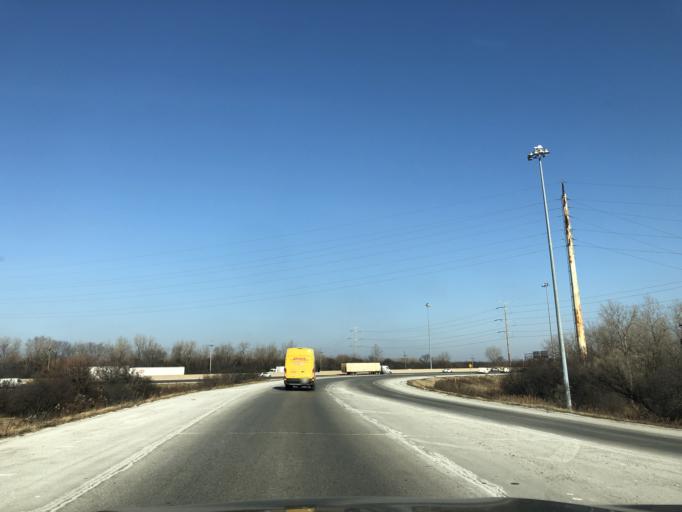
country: US
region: Illinois
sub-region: Cook County
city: Summit
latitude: 41.7943
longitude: -87.8175
